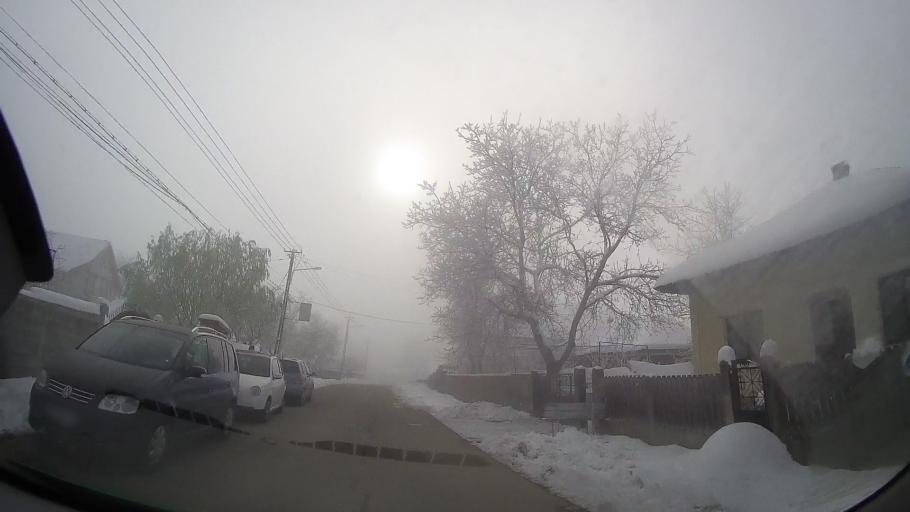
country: RO
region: Iasi
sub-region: Comuna Valea Seaca
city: Topile
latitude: 47.2628
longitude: 26.6673
